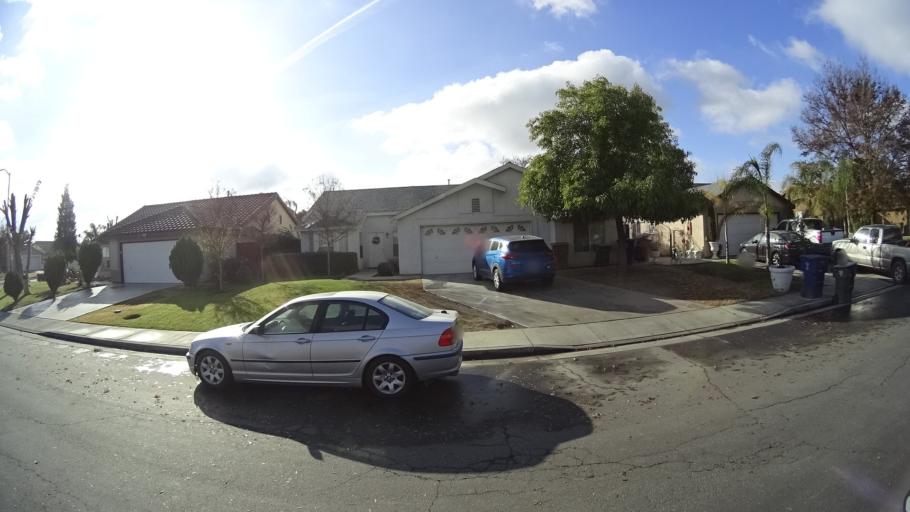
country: US
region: California
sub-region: Kern County
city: Greenfield
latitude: 35.2910
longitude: -119.0123
